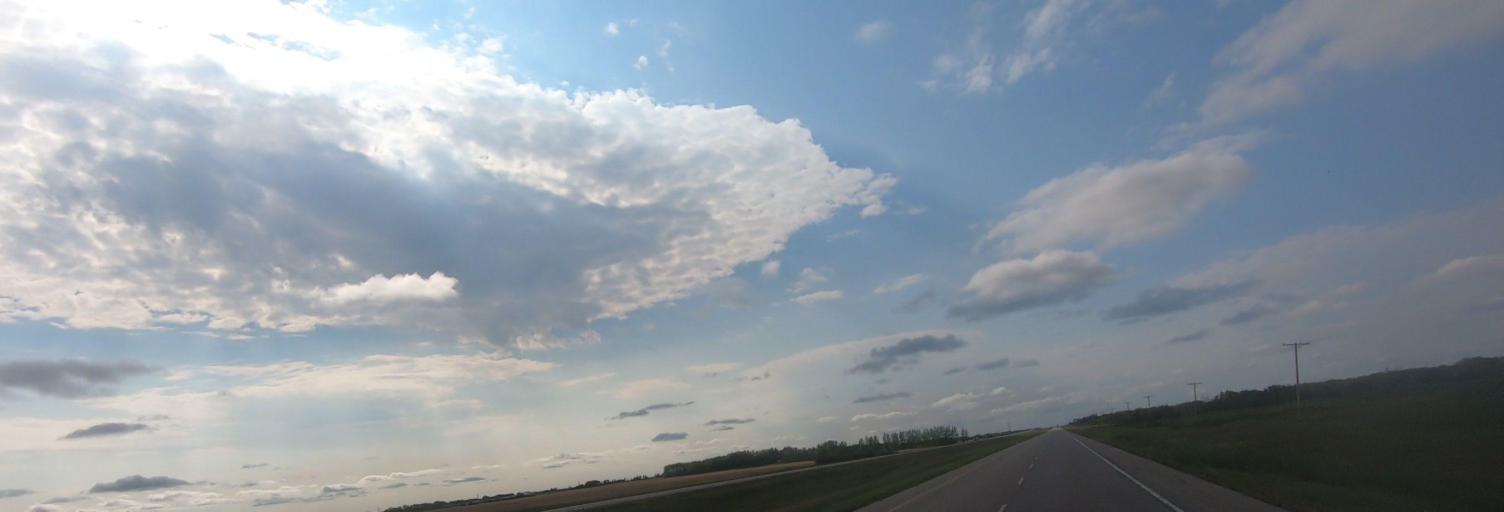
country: CA
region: Saskatchewan
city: Moosomin
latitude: 50.2299
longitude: -101.8544
